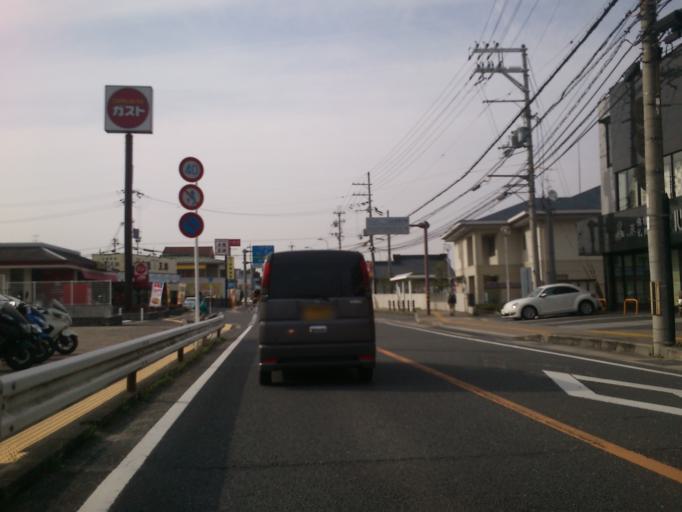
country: JP
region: Kyoto
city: Tanabe
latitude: 34.8129
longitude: 135.7717
